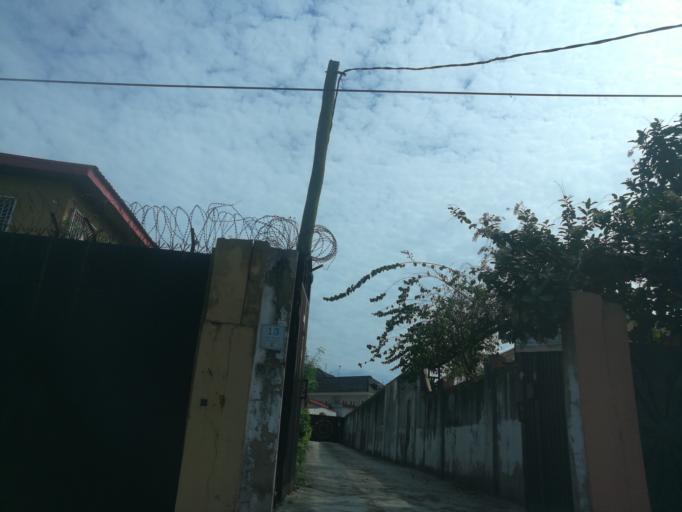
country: NG
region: Lagos
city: Ojota
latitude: 6.5777
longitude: 3.3658
